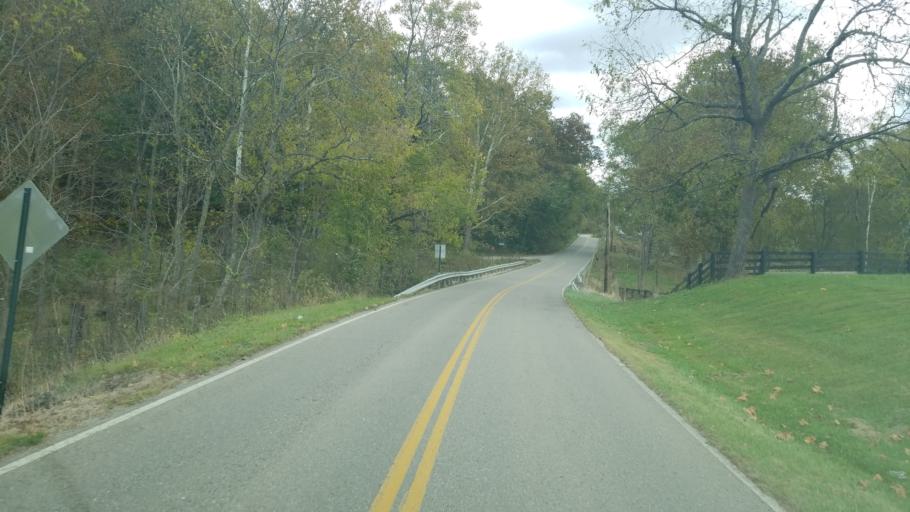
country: US
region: Ohio
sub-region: Jackson County
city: Jackson
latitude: 39.1456
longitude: -82.6614
